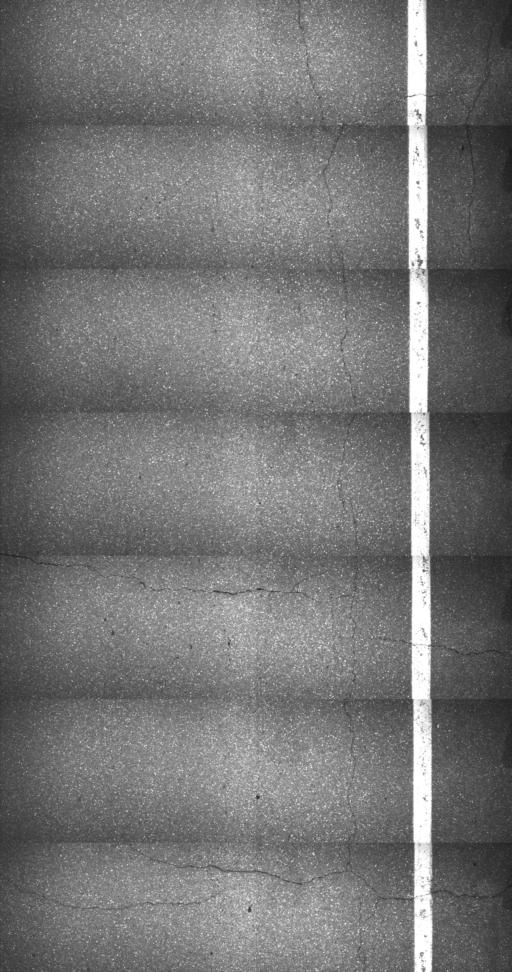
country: US
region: Vermont
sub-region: Caledonia County
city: Saint Johnsbury
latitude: 44.3725
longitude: -71.9095
